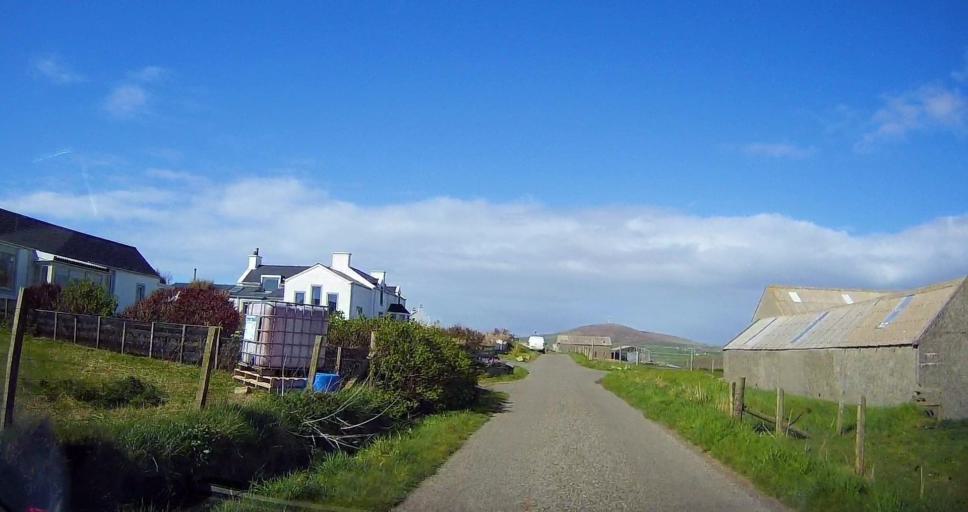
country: GB
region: Scotland
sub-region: Shetland Islands
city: Sandwick
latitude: 59.9066
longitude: -1.3348
